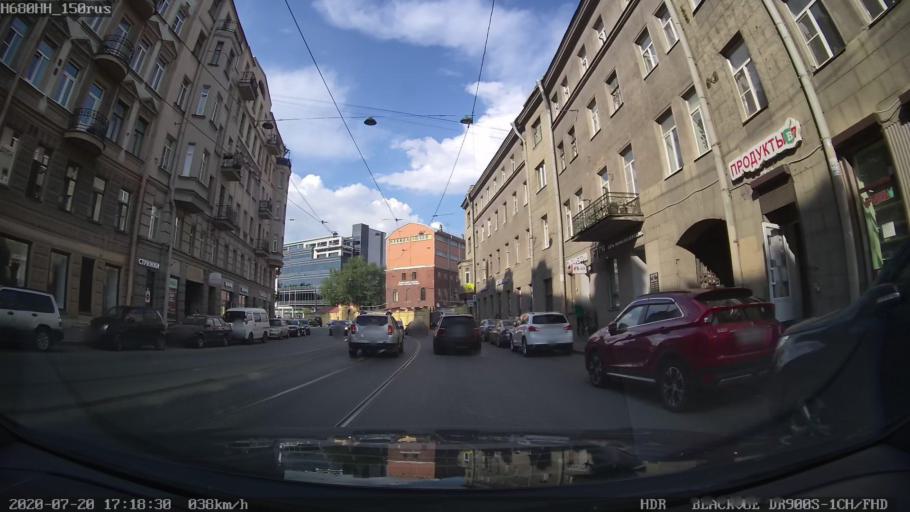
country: RU
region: St.-Petersburg
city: Admiralteisky
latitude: 59.9034
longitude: 30.2773
